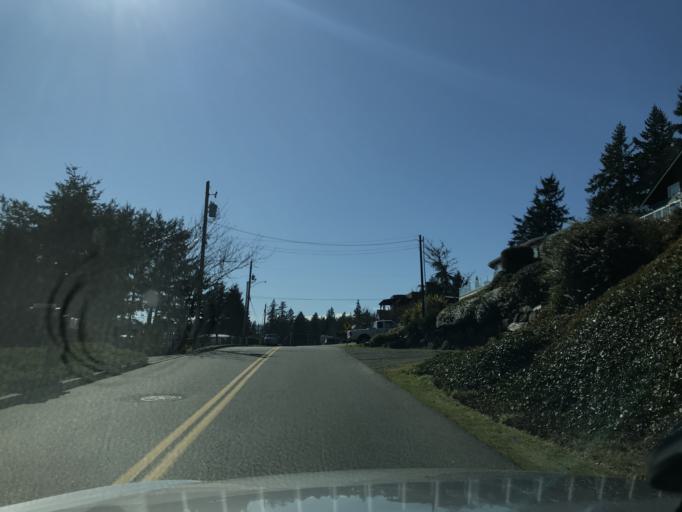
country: US
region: Washington
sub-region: Pierce County
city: Gig Harbor
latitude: 47.3402
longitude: -122.5903
